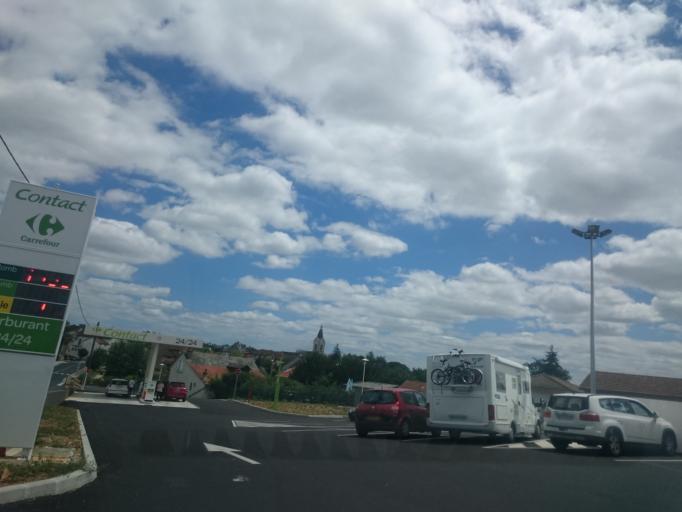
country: FR
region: Auvergne
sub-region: Departement du Cantal
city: Saint-Paul-des-Landes
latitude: 44.9447
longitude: 2.3110
